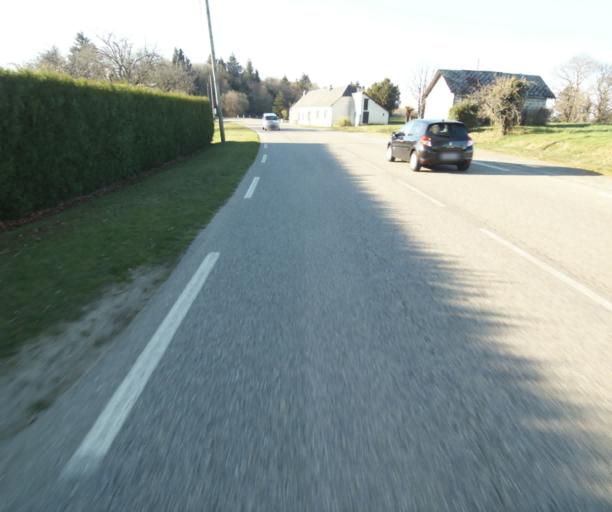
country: FR
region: Limousin
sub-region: Departement de la Correze
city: Seilhac
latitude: 45.3798
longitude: 1.7226
